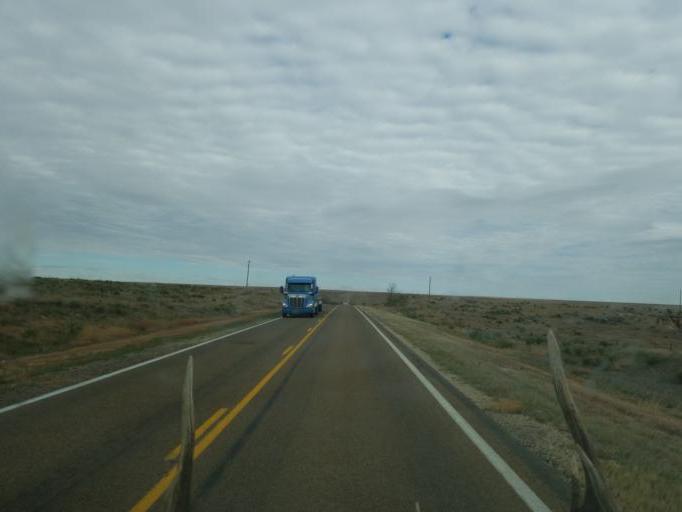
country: US
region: Kansas
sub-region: Wallace County
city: Sharon Springs
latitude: 39.0133
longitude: -101.3583
